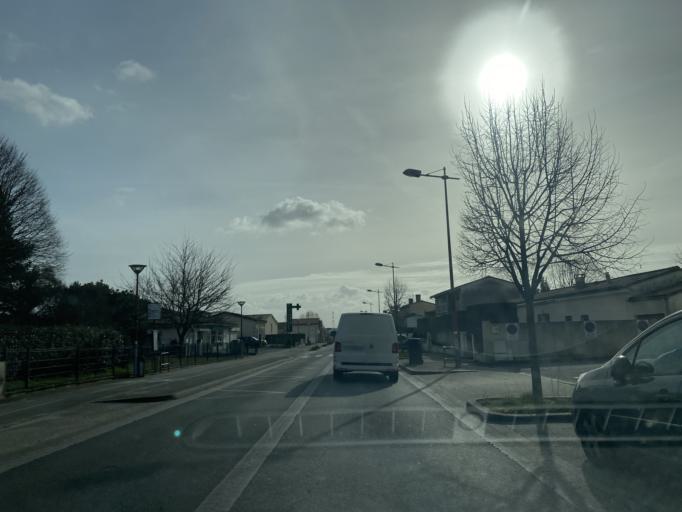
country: FR
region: Aquitaine
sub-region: Departement de la Gironde
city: Le Taillan-Medoc
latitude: 44.9081
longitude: -0.6690
